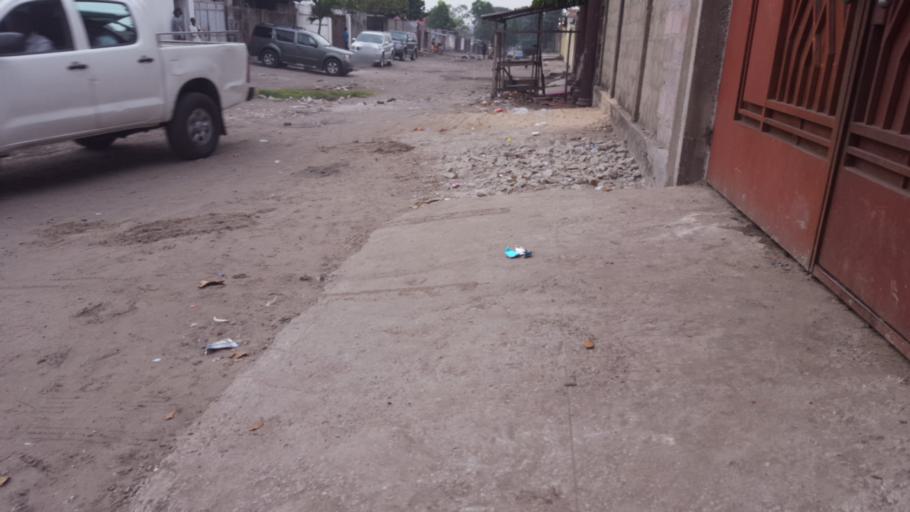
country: CD
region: Kinshasa
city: Masina
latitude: -4.3842
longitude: 15.3544
